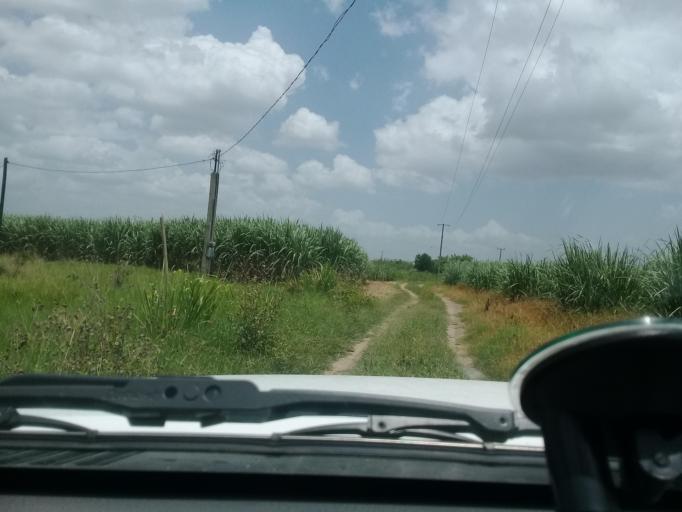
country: MX
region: Veracruz
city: Moralillo
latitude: 22.1329
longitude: -98.0376
